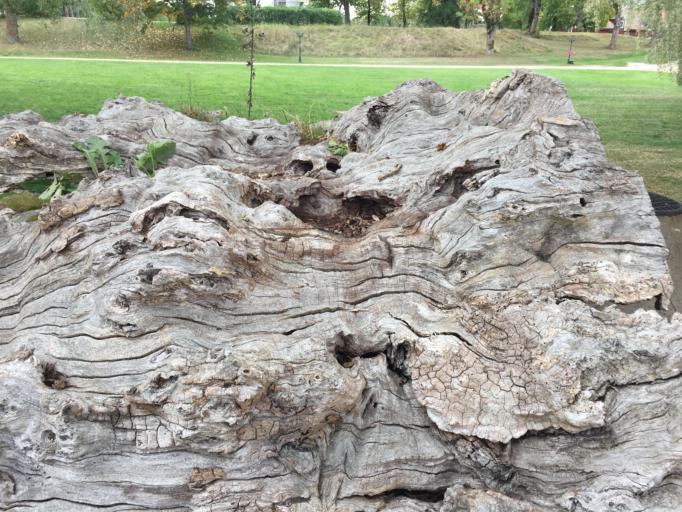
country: SE
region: Stockholm
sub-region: Nynashamns Kommun
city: Osmo
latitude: 59.0395
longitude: 18.0159
